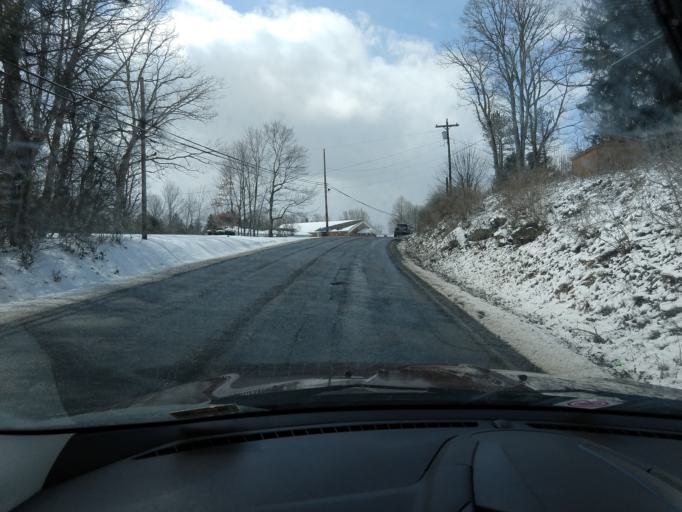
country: US
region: West Virginia
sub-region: Nicholas County
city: Craigsville
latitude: 38.3310
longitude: -80.6459
